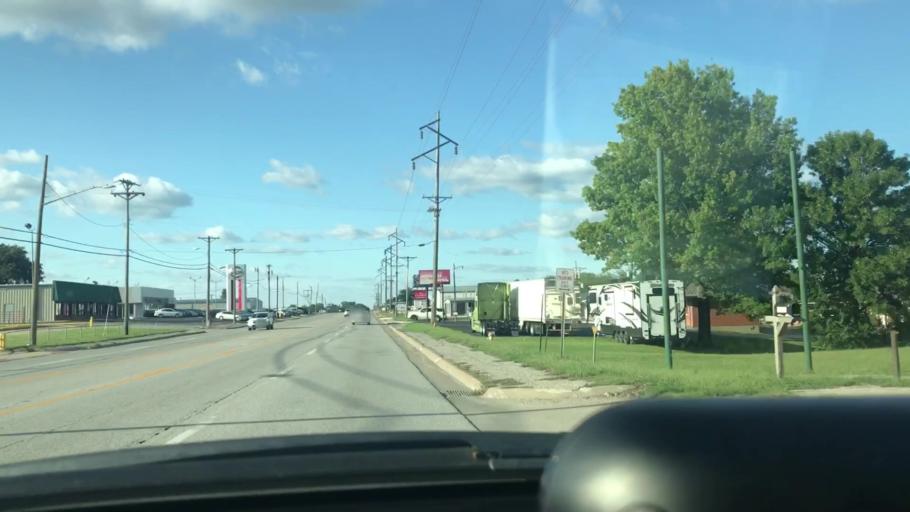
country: US
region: Missouri
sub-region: Pettis County
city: Sedalia
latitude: 38.6785
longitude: -93.2514
